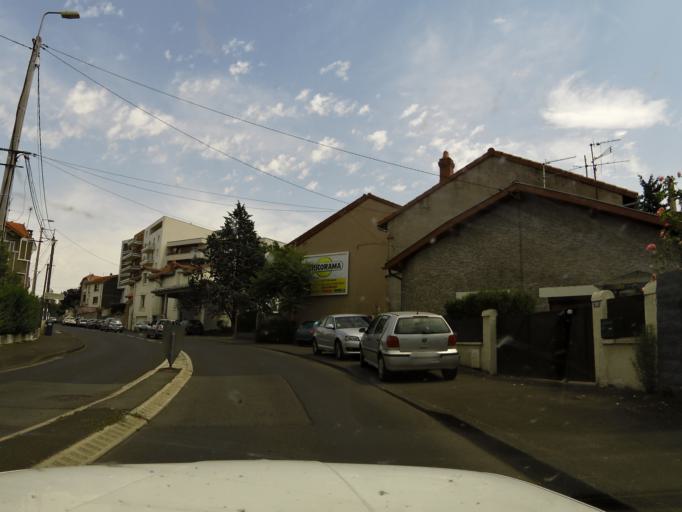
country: FR
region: Auvergne
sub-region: Departement du Puy-de-Dome
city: Beaumont
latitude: 45.7573
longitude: 3.0812
